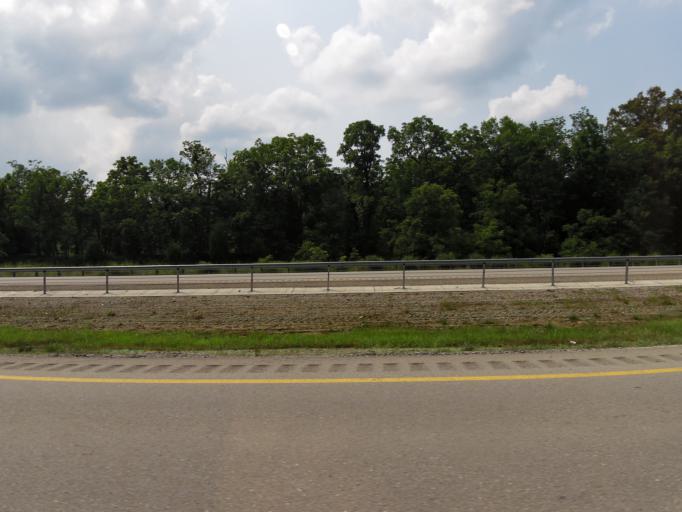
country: US
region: Kentucky
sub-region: Boone County
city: Verona
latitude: 38.8037
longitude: -84.7277
